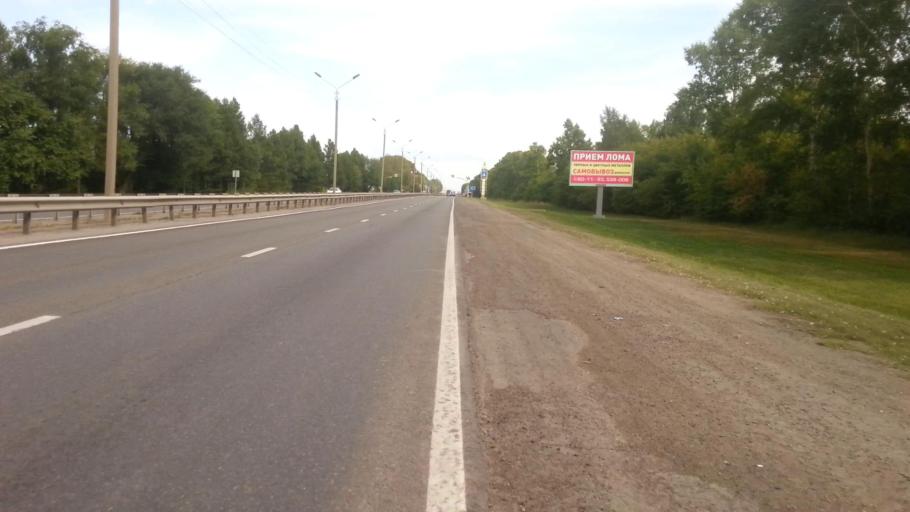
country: RU
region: Altai Krai
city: Vlasikha
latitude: 53.3529
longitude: 83.5635
